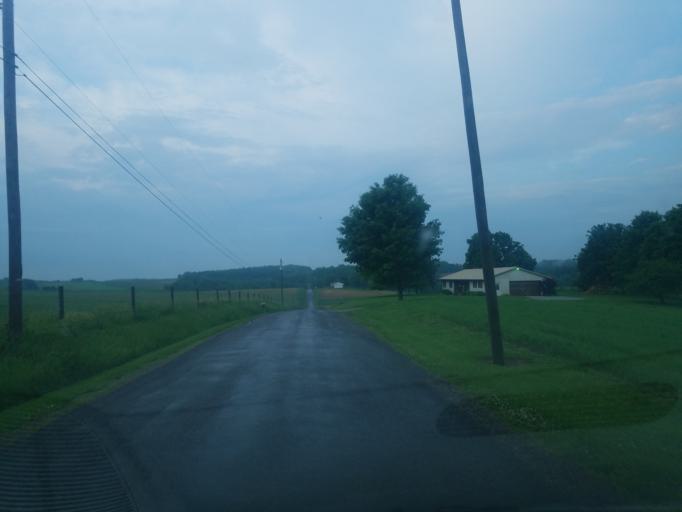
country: US
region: Ohio
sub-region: Mahoning County
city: Sebring
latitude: 40.7834
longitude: -80.9556
